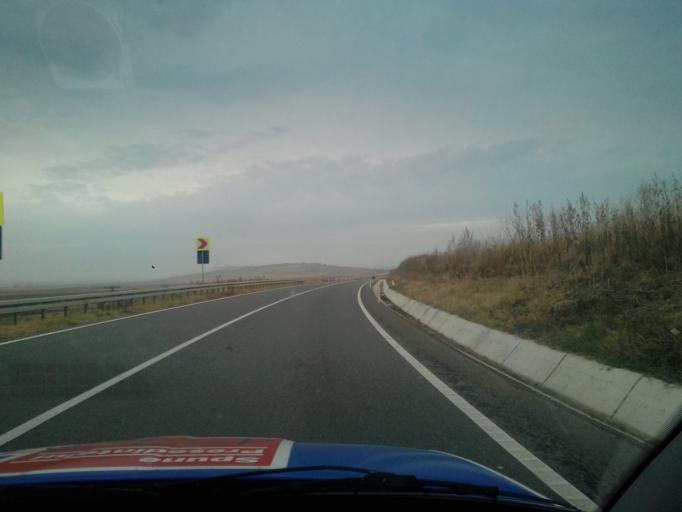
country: RO
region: Vaslui
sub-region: Comuna Albesti
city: Corni-Albesti
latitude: 46.5381
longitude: 27.8393
